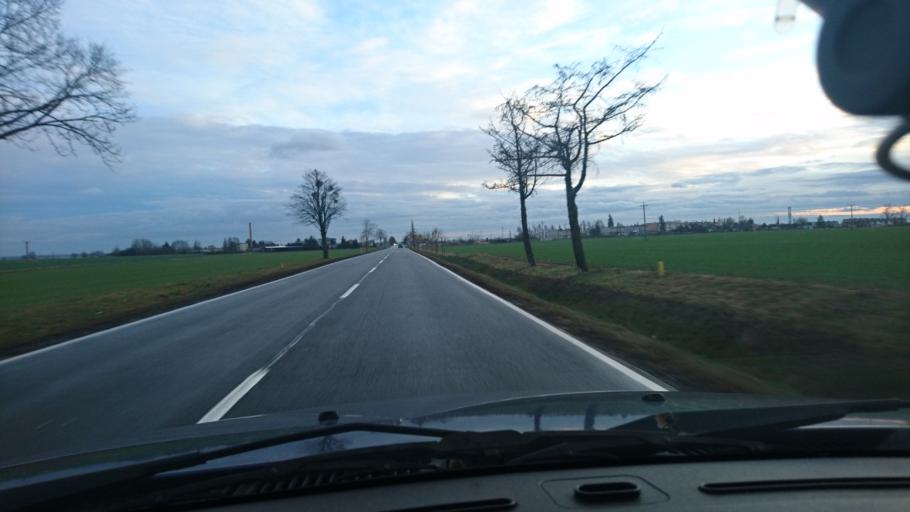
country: PL
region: Opole Voivodeship
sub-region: Powiat kluczborski
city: Kluczbork
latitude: 50.9994
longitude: 18.2066
